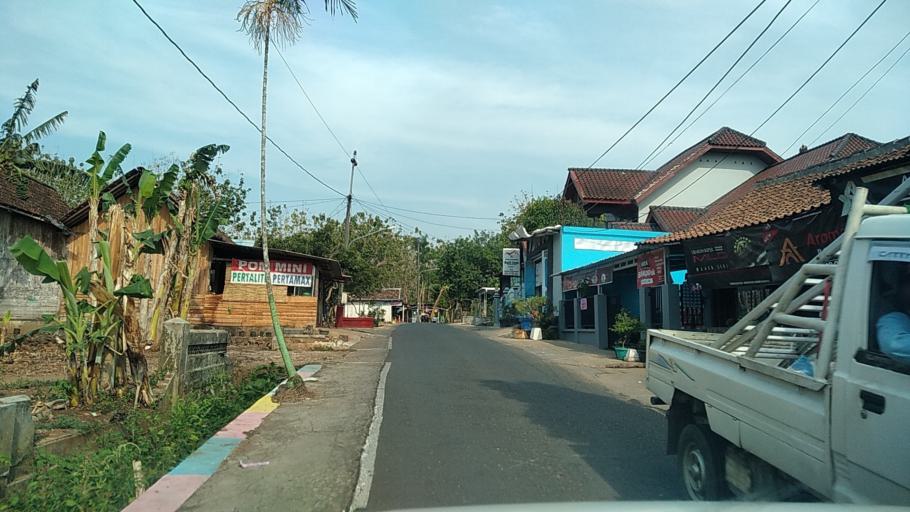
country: ID
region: Central Java
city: Semarang
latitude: -7.0407
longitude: 110.3048
